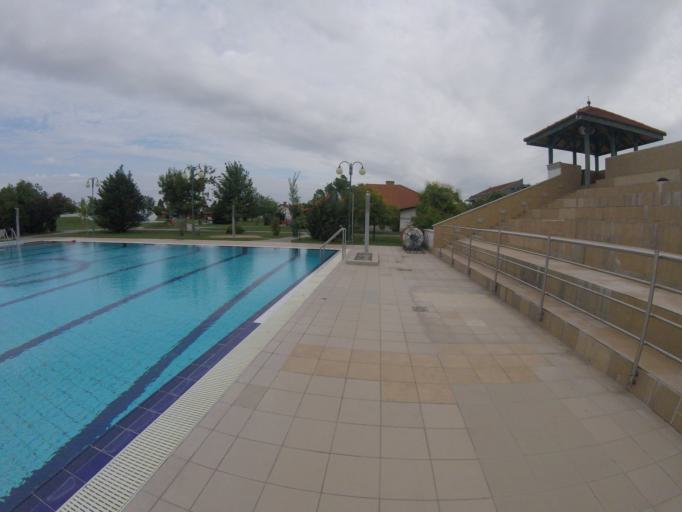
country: HU
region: Pest
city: Cegled
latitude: 47.2003
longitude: 19.7351
